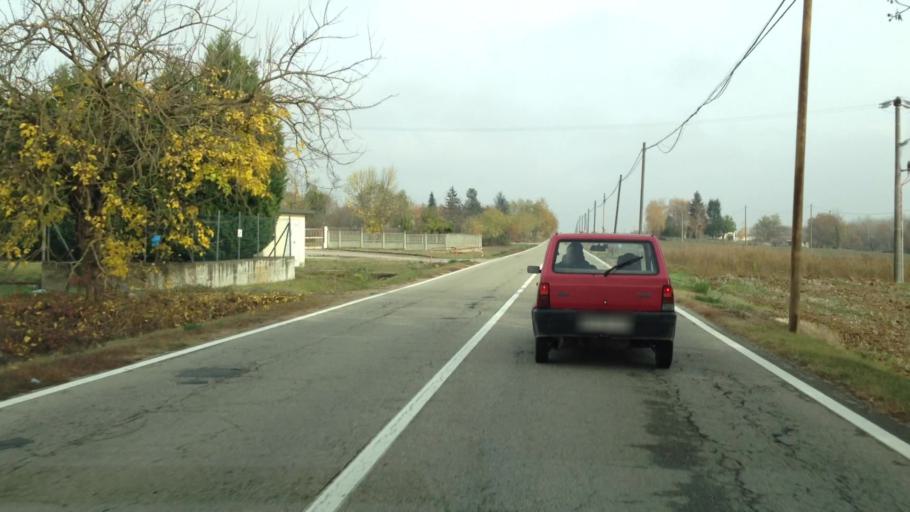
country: IT
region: Piedmont
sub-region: Provincia di Asti
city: Cerro Tanaro
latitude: 44.8844
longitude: 8.3543
